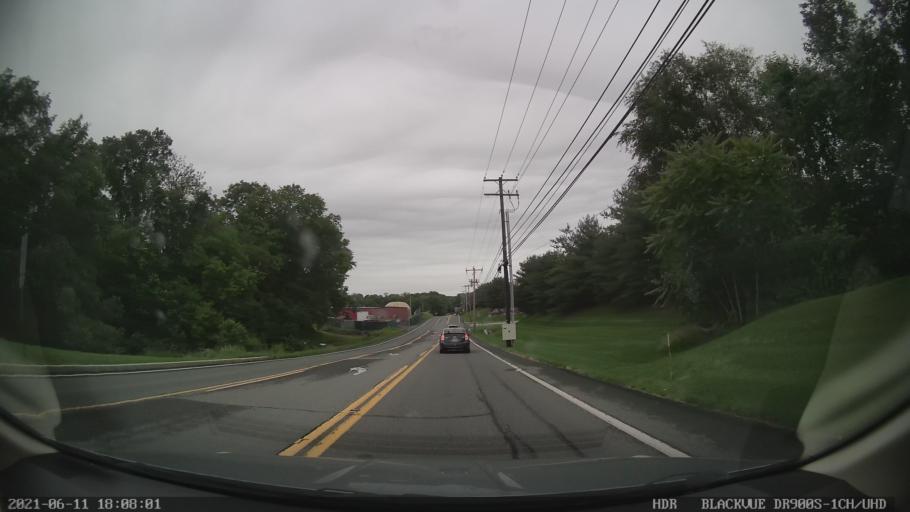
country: US
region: Pennsylvania
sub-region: Berks County
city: Whitfield
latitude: 40.3461
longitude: -76.0031
